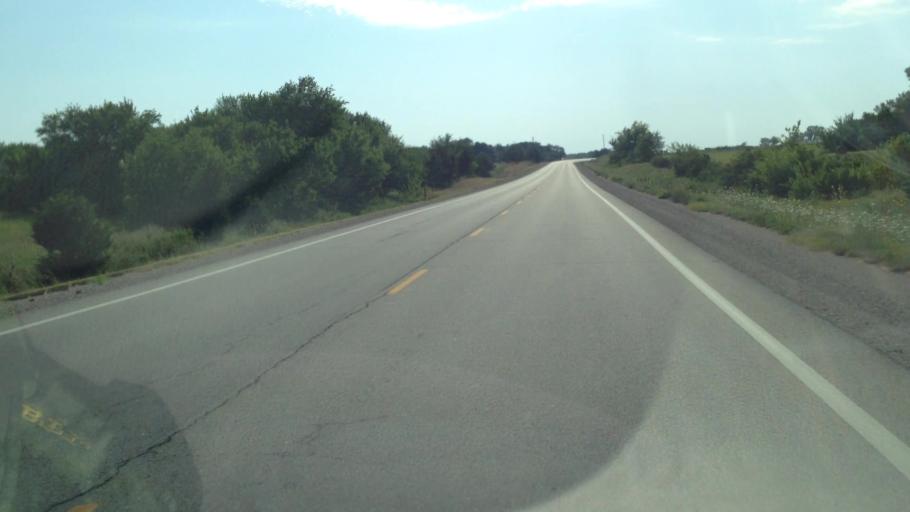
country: US
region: Kansas
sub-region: Anderson County
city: Garnett
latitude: 38.0817
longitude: -95.2332
